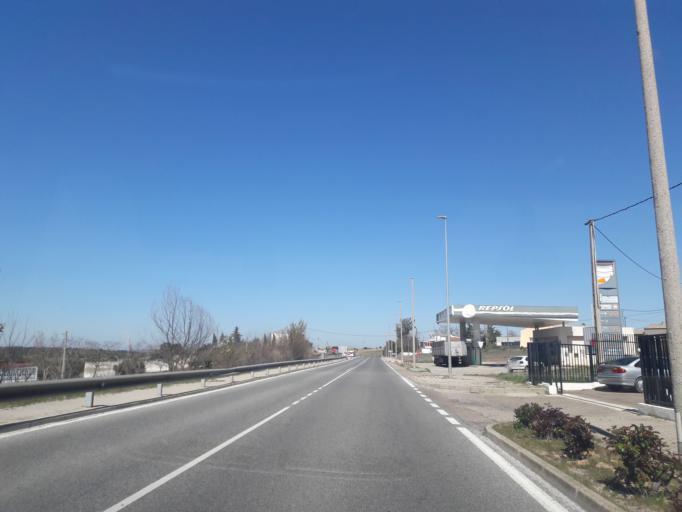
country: ES
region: Castille and Leon
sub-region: Provincia de Salamanca
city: Mozarbez
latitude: 40.8591
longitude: -5.6519
